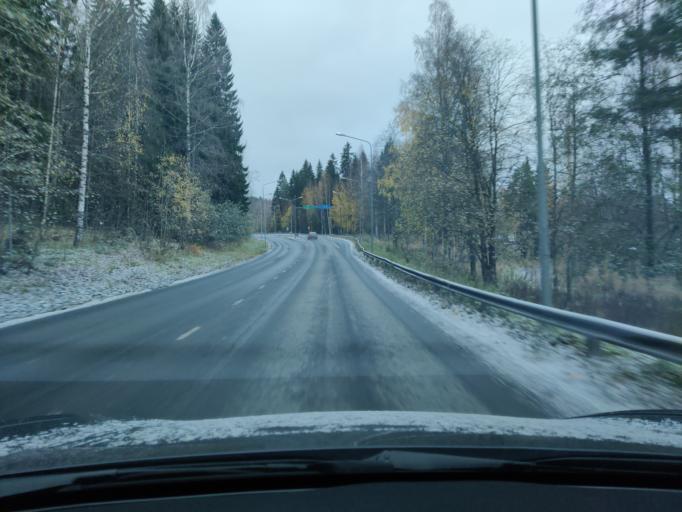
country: FI
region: Northern Savo
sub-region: Kuopio
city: Kuopio
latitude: 62.8434
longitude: 27.6305
